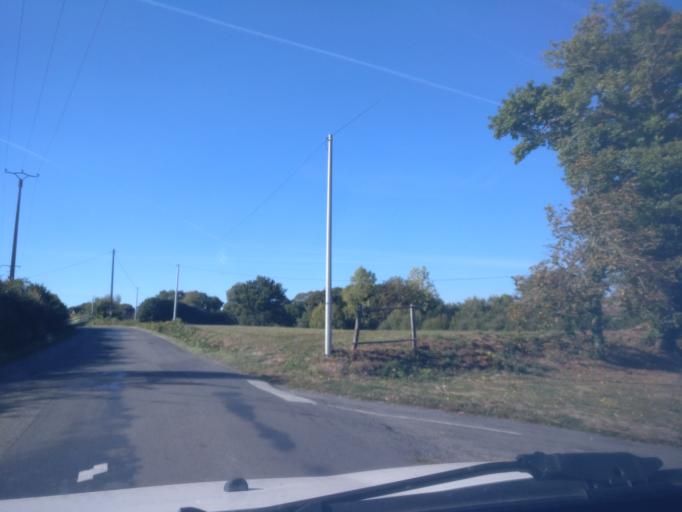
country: FR
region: Brittany
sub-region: Departement d'Ille-et-Vilaine
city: Chevaigne
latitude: 48.2104
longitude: -1.6458
